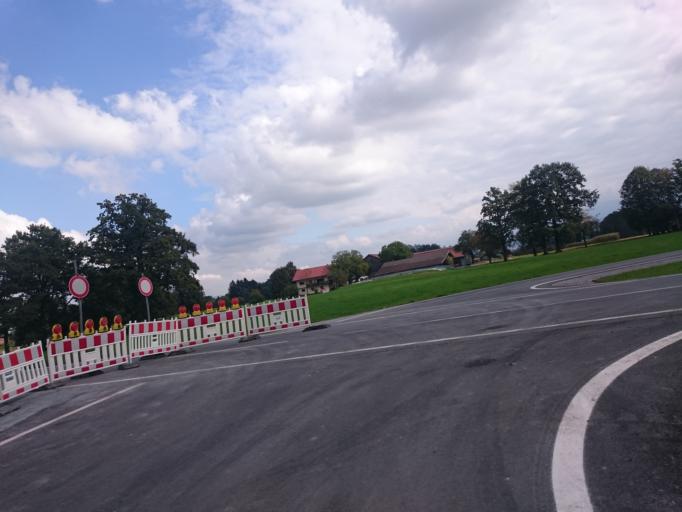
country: DE
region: Bavaria
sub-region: Upper Bavaria
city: Kolbermoor
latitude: 47.8170
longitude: 12.0678
